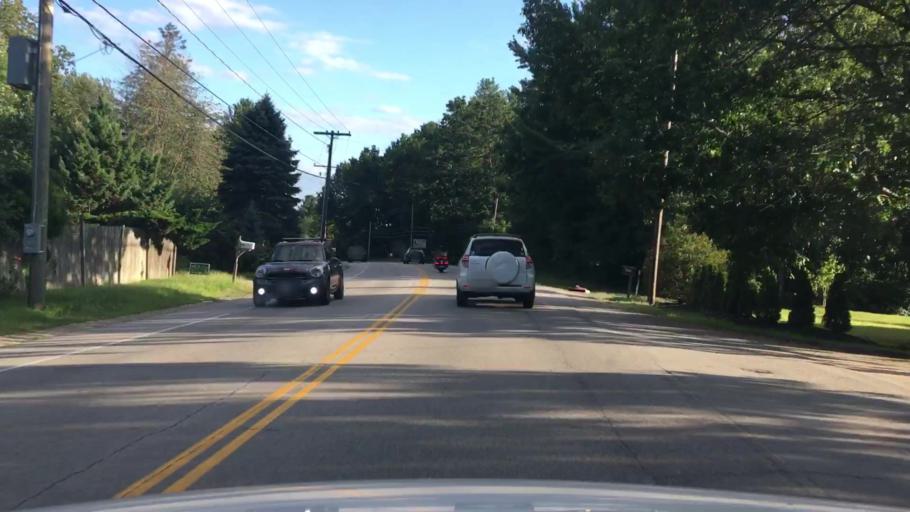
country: US
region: Maine
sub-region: York County
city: Eliot
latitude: 43.1417
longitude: -70.8386
